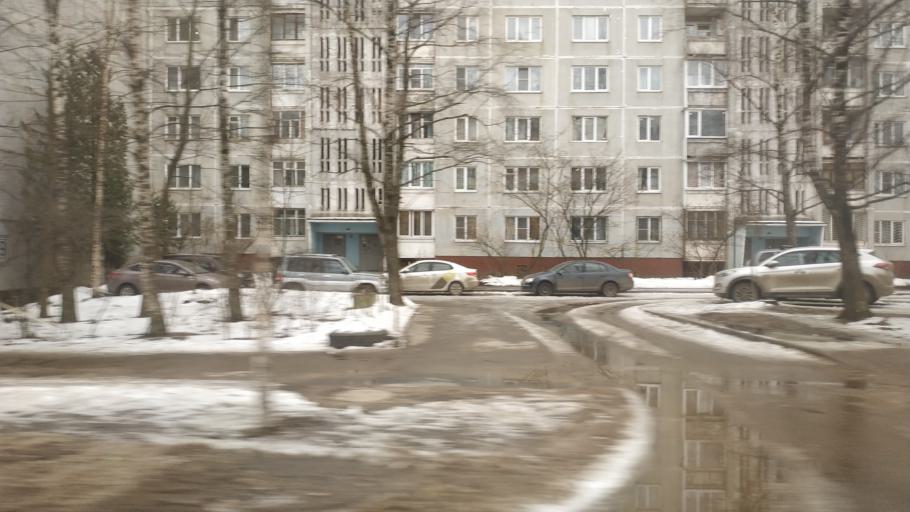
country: RU
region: Tverskaya
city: Tver
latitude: 56.8870
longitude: 35.8371
